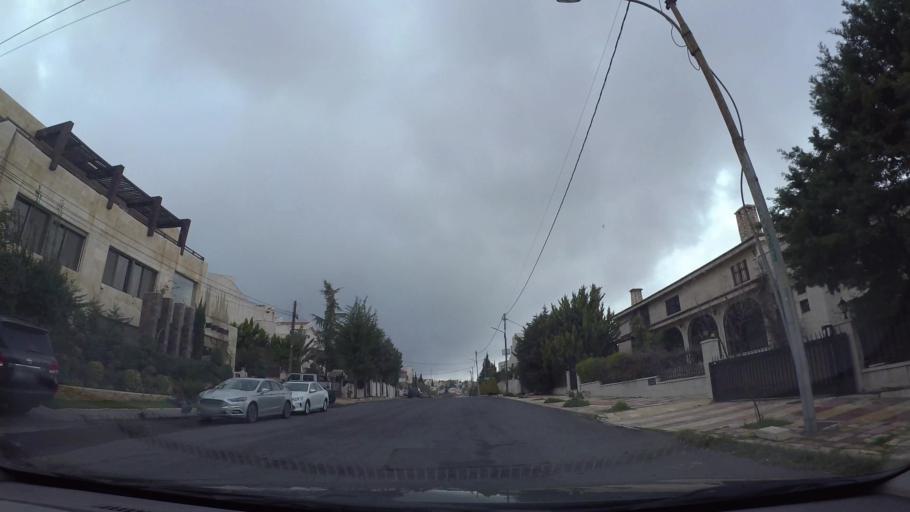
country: JO
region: Amman
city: Amman
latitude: 31.9498
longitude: 35.8958
